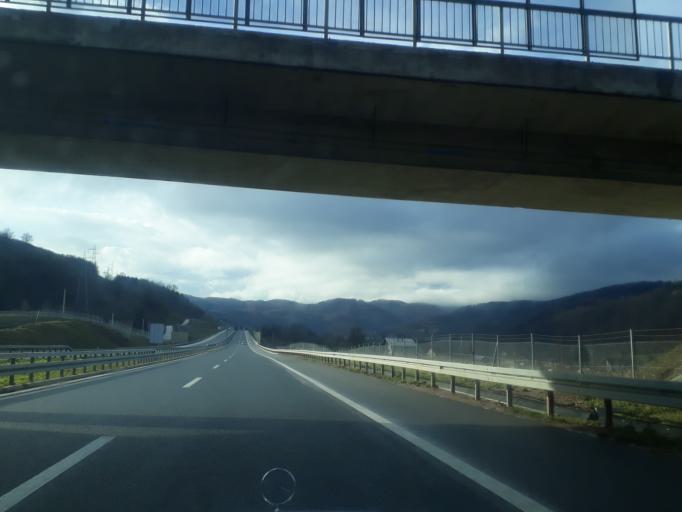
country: BA
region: Federation of Bosnia and Herzegovina
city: Polje
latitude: 43.8577
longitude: 18.1380
